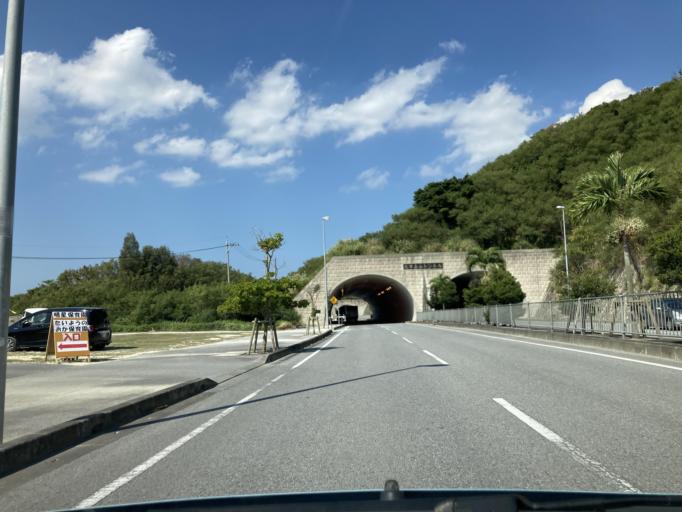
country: JP
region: Okinawa
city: Tomigusuku
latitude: 26.1861
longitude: 127.7207
